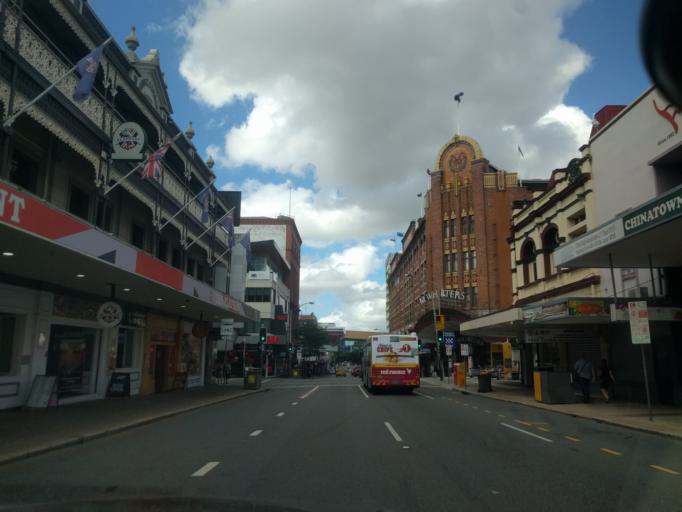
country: AU
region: Queensland
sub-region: Brisbane
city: Fortitude Valley
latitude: -27.4578
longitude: 153.0333
